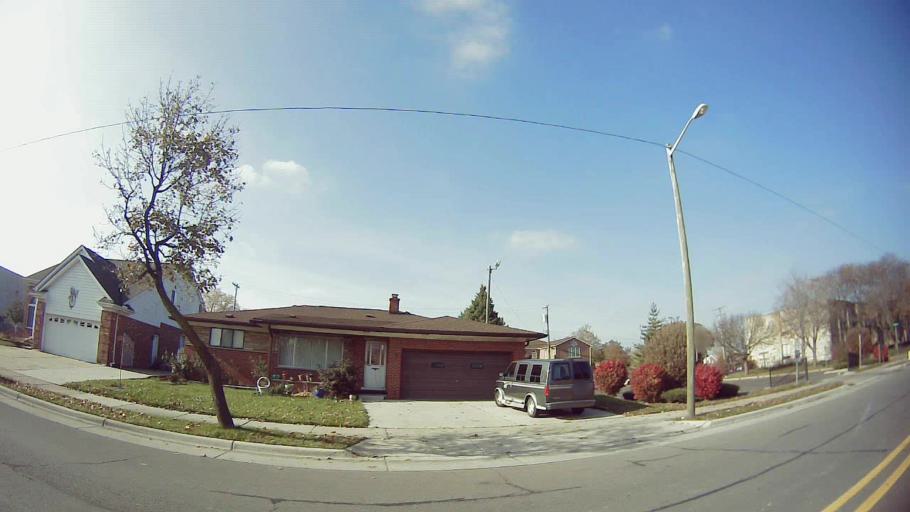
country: US
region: Michigan
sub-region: Wayne County
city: Dearborn
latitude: 42.3504
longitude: -83.1868
